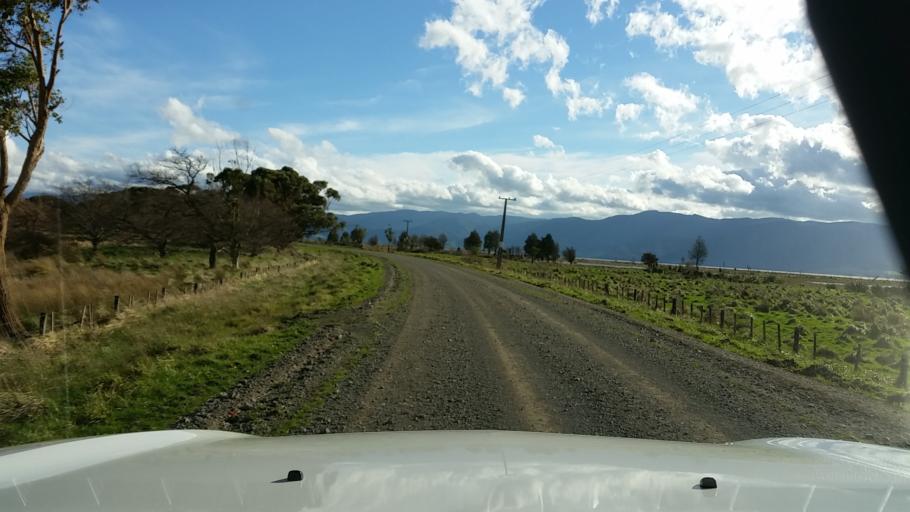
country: NZ
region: Wellington
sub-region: Upper Hutt City
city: Upper Hutt
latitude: -41.2420
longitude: 175.2685
